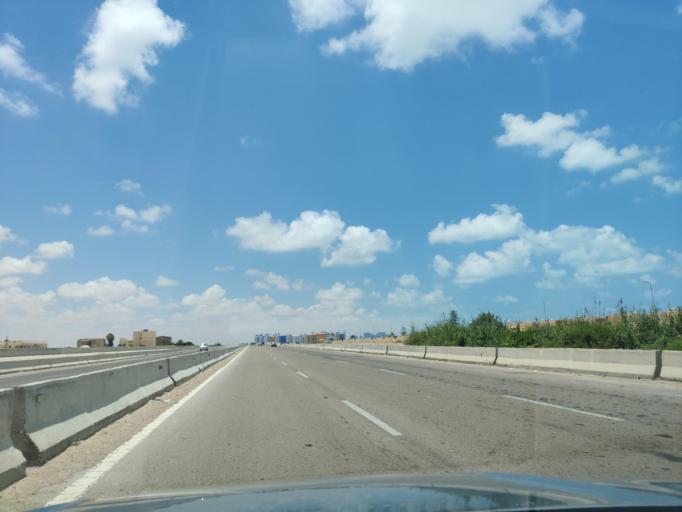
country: EG
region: Muhafazat Matruh
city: Al `Alamayn
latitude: 30.8195
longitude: 29.0213
